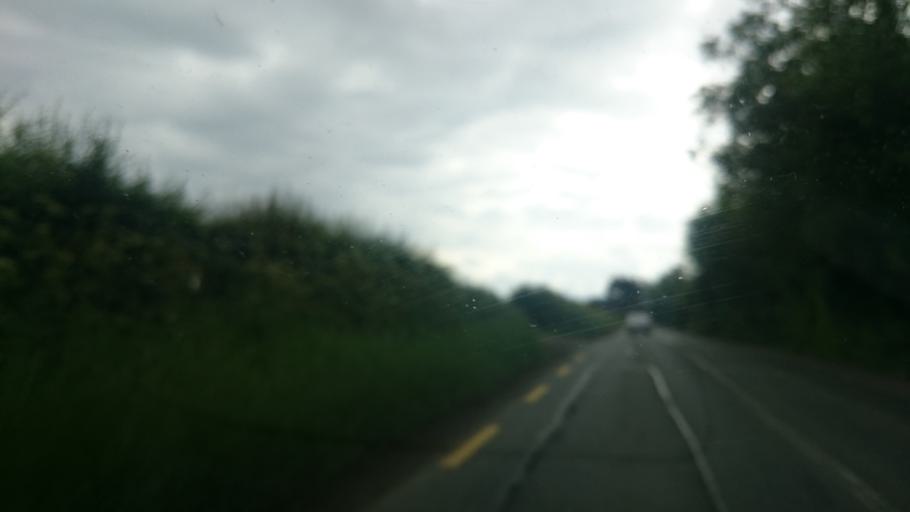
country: IE
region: Leinster
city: Lusk
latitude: 53.5130
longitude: -6.1758
